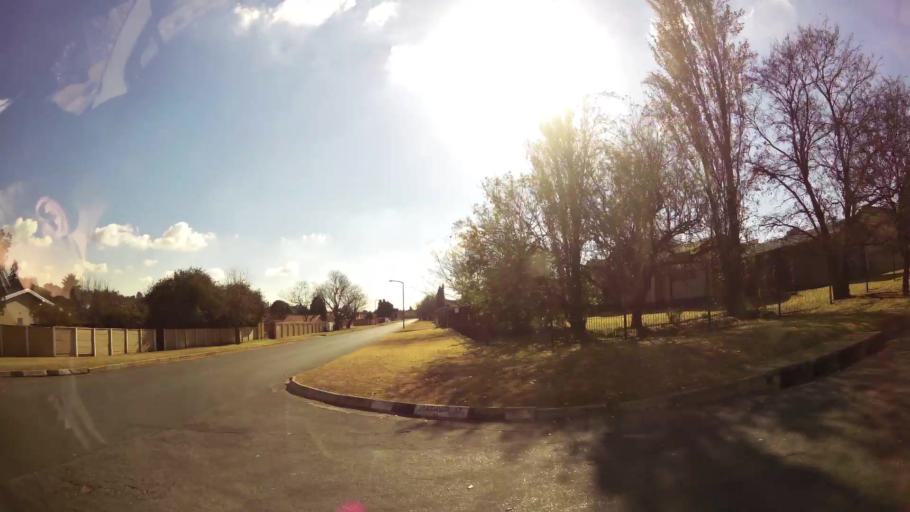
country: ZA
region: Gauteng
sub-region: City of Johannesburg Metropolitan Municipality
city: Roodepoort
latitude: -26.1446
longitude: 27.8214
